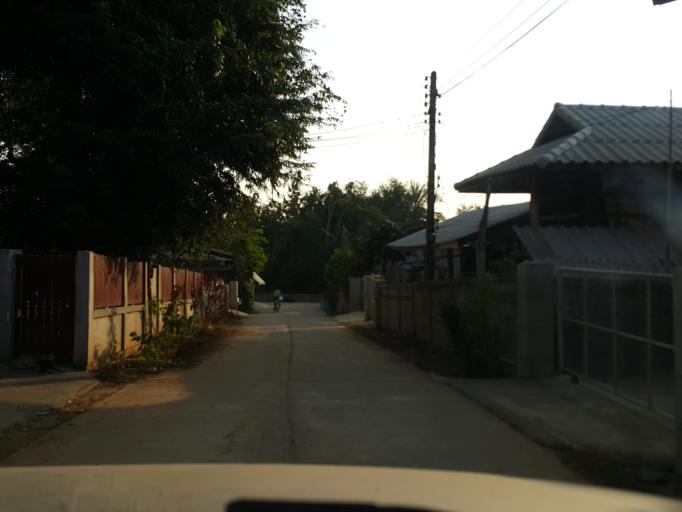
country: TH
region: Lamphun
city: Ban Thi
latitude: 18.5984
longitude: 99.2814
